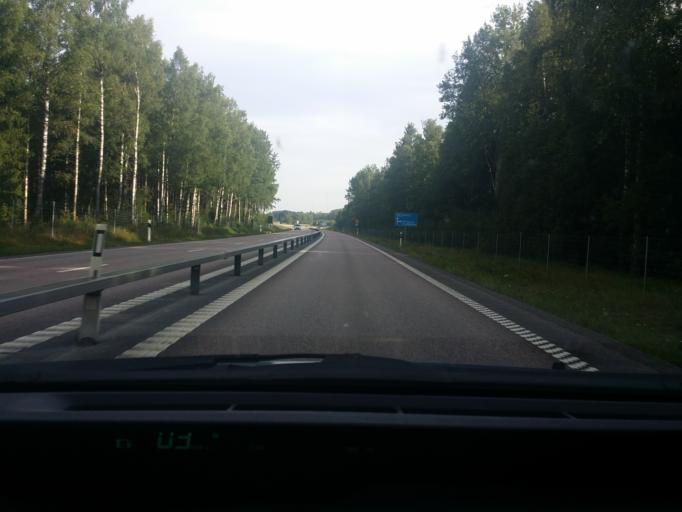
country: SE
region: Vaestmanland
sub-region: Vasteras
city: Hokasen
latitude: 59.6715
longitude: 16.5826
